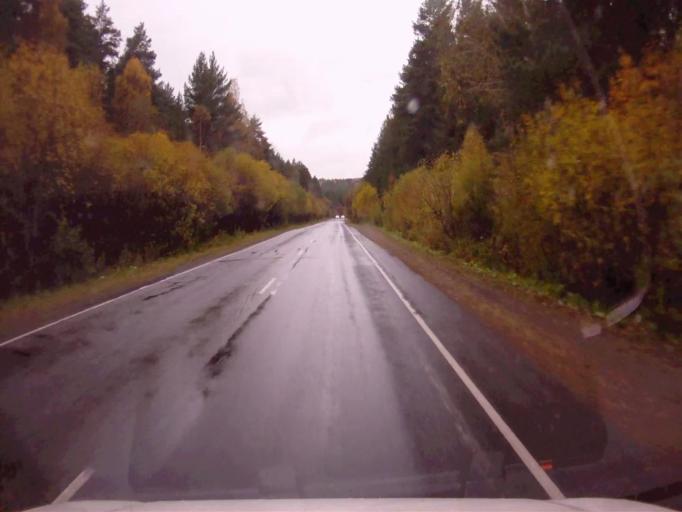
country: RU
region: Chelyabinsk
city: Verkhniy Ufaley
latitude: 56.0492
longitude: 60.1441
